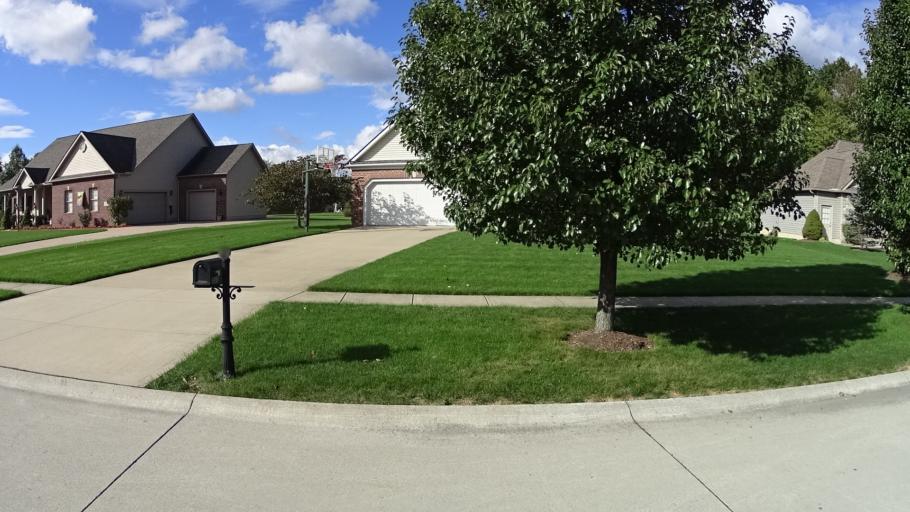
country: US
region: Ohio
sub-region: Lorain County
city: Grafton
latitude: 41.2910
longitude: -82.0623
